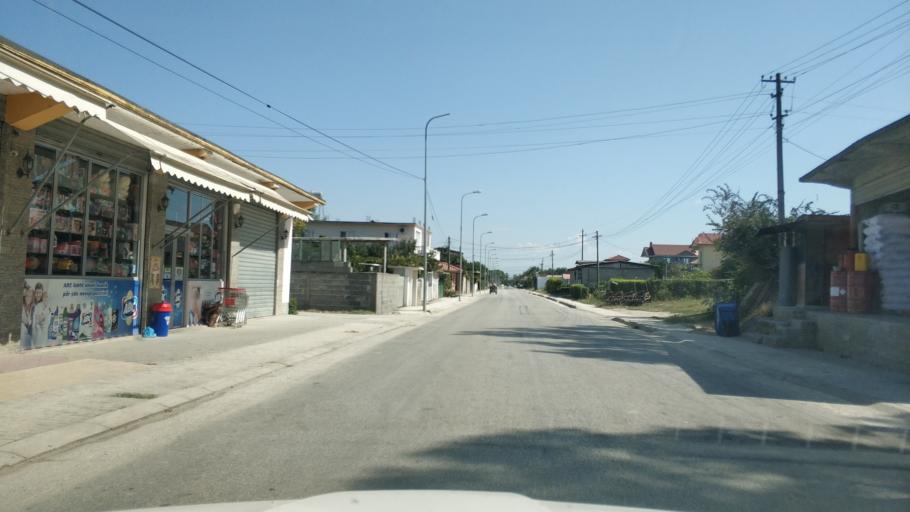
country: AL
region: Fier
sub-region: Rrethi i Lushnjes
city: Gradishte
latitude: 40.8935
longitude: 19.6232
